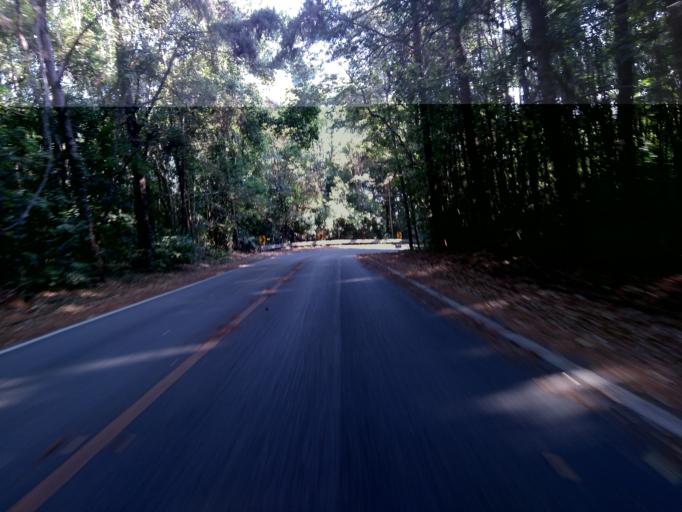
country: TH
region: Chiang Mai
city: Chiang Mai
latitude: 18.8035
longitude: 98.9056
